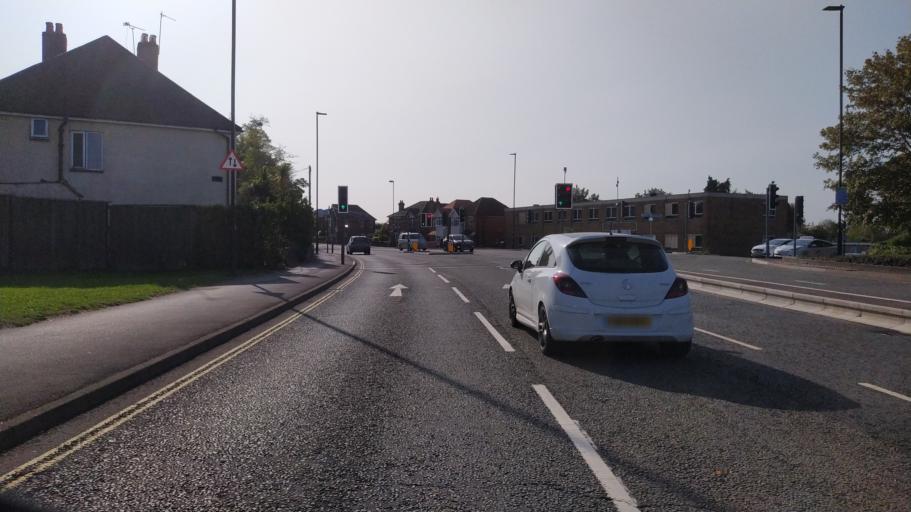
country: GB
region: England
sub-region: Hampshire
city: West End
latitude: 50.9139
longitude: -1.3564
